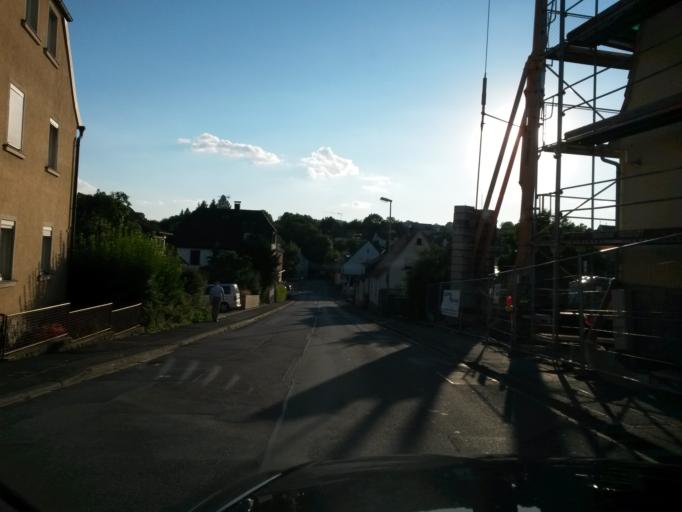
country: DE
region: Bavaria
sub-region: Regierungsbezirk Unterfranken
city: Rimpar
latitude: 49.8524
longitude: 9.9626
